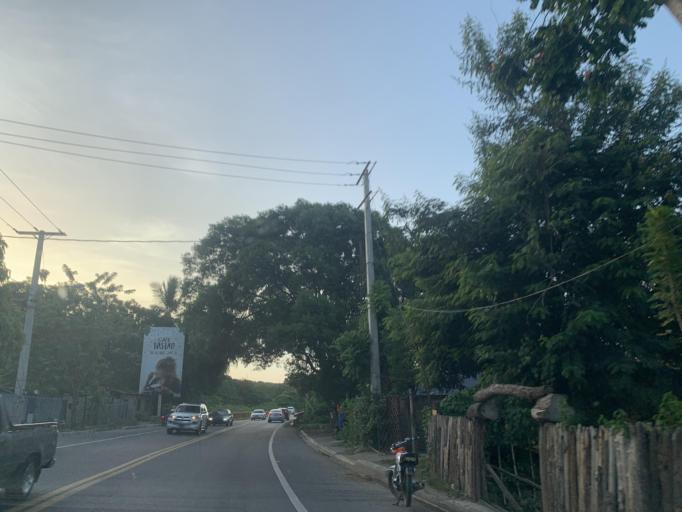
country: DO
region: Puerto Plata
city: Imbert
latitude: 19.7353
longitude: -70.8348
